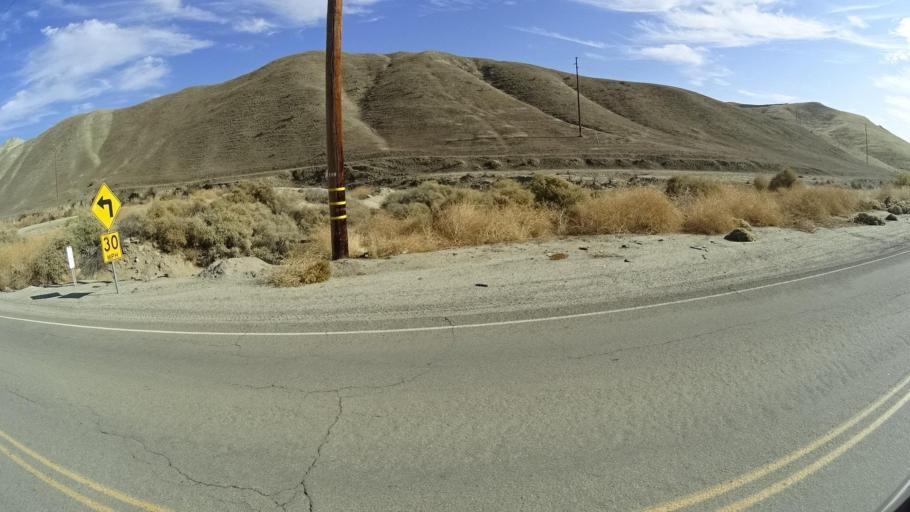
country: US
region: California
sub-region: Kern County
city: Oildale
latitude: 35.5611
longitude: -118.9562
